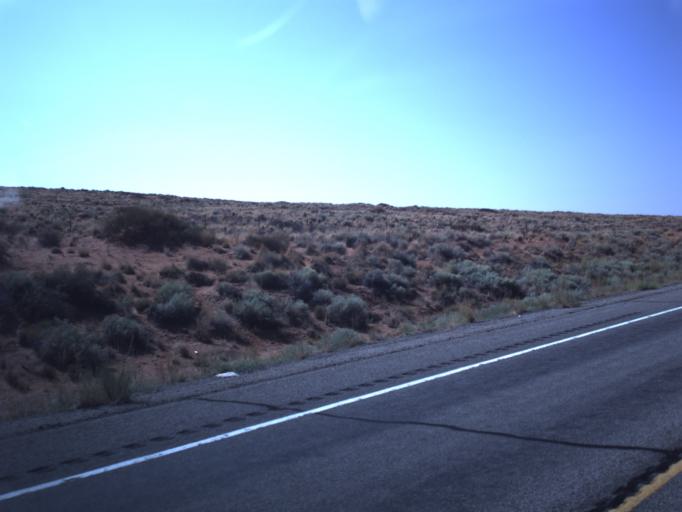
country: US
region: Utah
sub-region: San Juan County
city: Blanding
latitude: 37.2323
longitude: -109.6140
